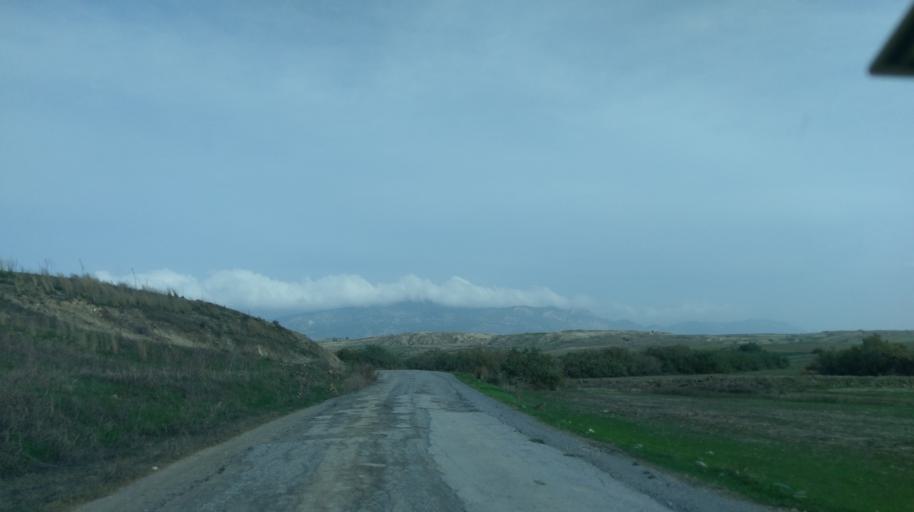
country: CY
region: Keryneia
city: Lapithos
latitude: 35.2621
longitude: 33.0932
